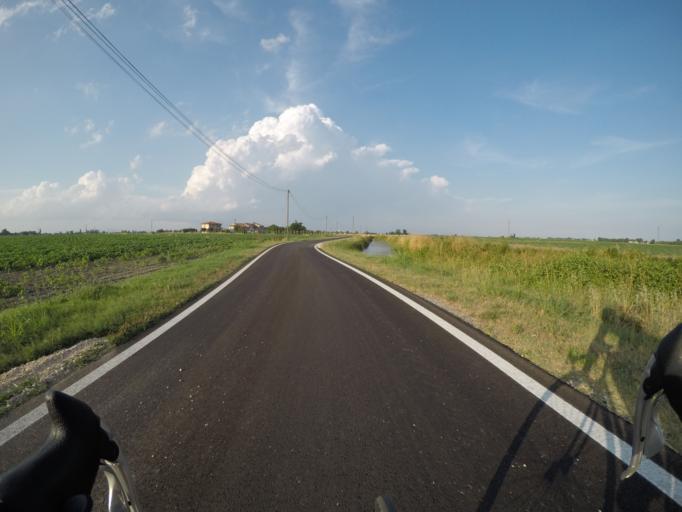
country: IT
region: Veneto
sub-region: Provincia di Rovigo
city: San Bellino
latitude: 45.0365
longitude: 11.5871
